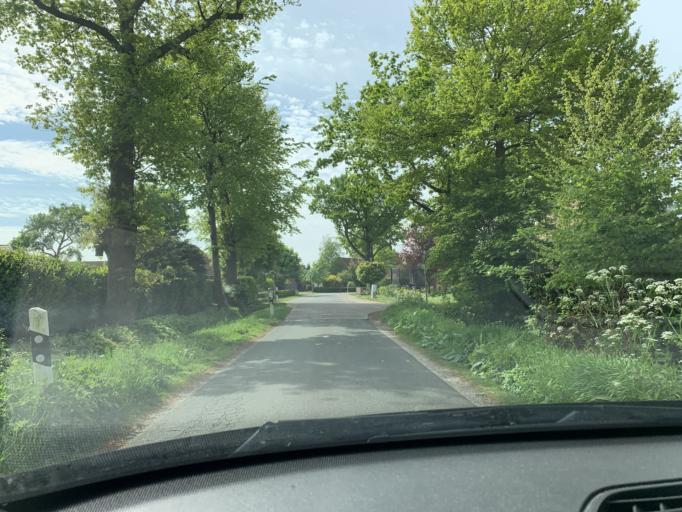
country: DE
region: Lower Saxony
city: Apen
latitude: 53.2266
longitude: 7.8136
